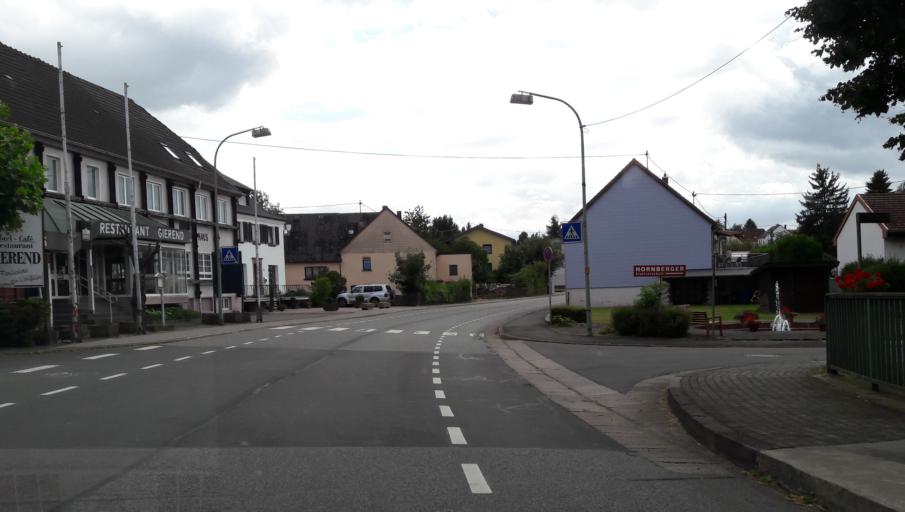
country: DE
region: Saarland
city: Oberthal
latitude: 49.5645
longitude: 7.0922
